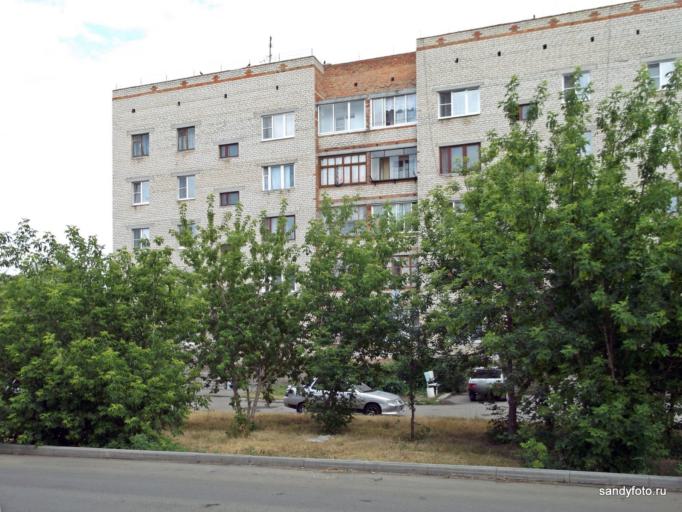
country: RU
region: Chelyabinsk
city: Troitsk
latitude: 54.0758
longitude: 61.5381
